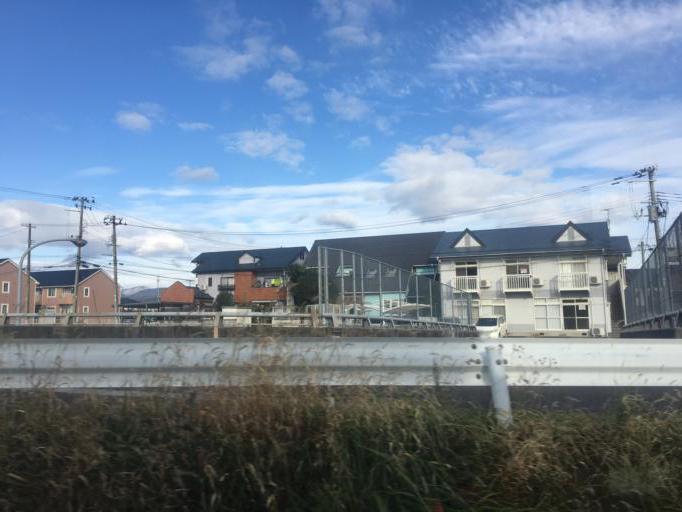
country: JP
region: Fukushima
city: Fukushima-shi
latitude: 37.7972
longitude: 140.4842
